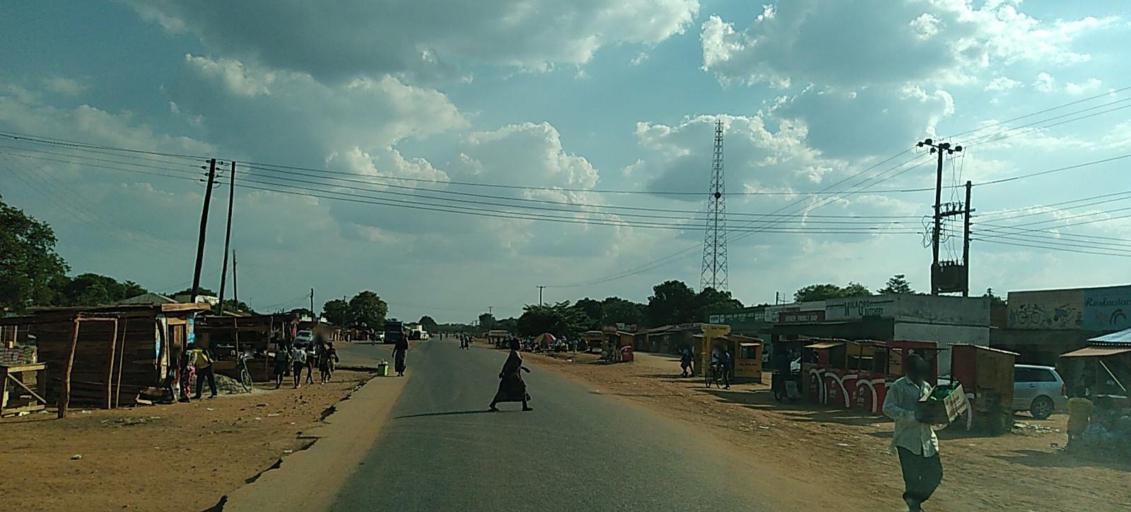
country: ZM
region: Copperbelt
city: Luanshya
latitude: -13.3556
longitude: 28.4159
